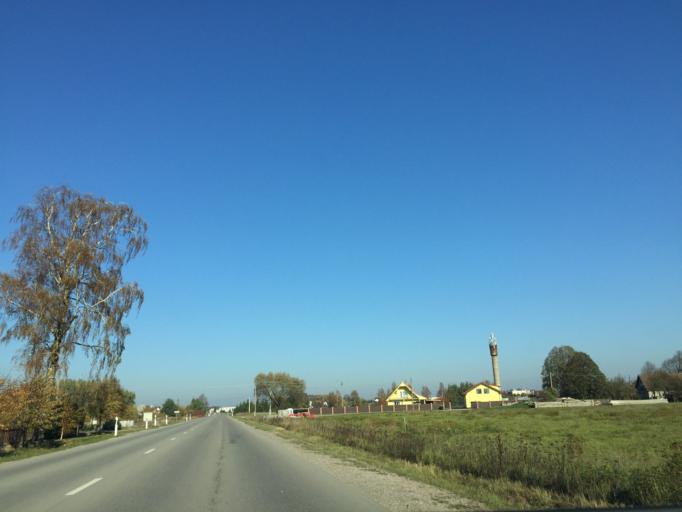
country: LT
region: Klaipedos apskritis
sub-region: Klaipeda
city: Klaipeda
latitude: 55.7517
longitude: 21.1925
